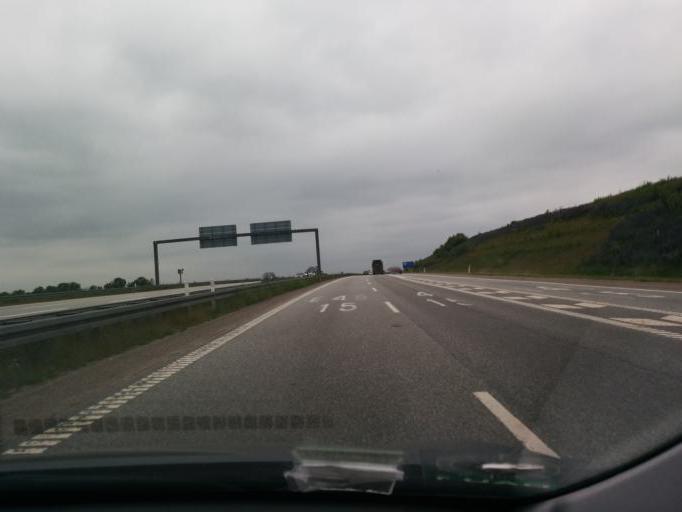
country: DK
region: Central Jutland
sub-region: Arhus Kommune
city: Trige
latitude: 56.2136
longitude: 10.1461
